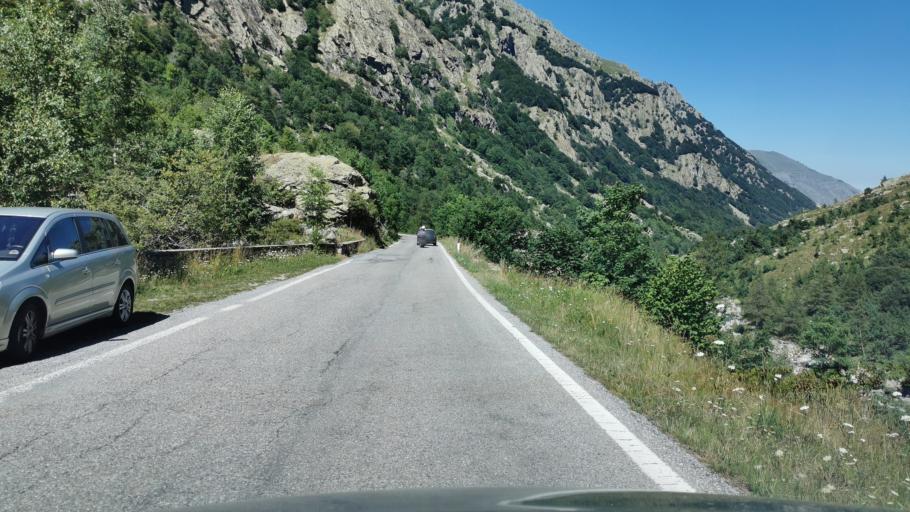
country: IT
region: Piedmont
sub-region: Provincia di Cuneo
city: Demonte
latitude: 44.2127
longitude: 7.2780
